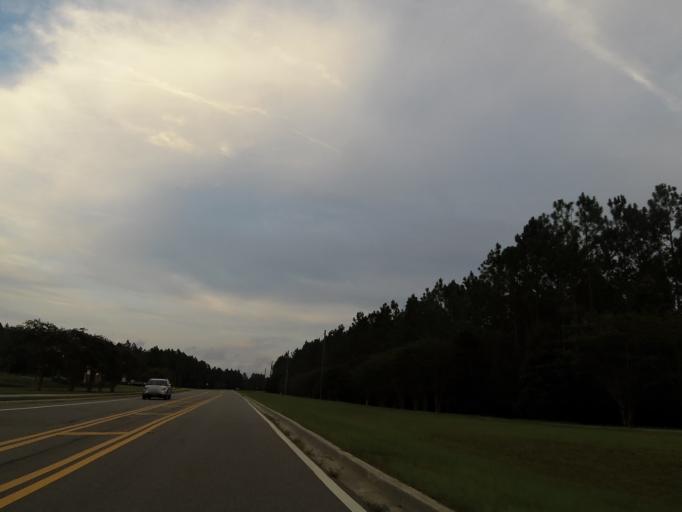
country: US
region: Florida
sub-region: Saint Johns County
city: Fruit Cove
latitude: 30.0859
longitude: -81.5737
